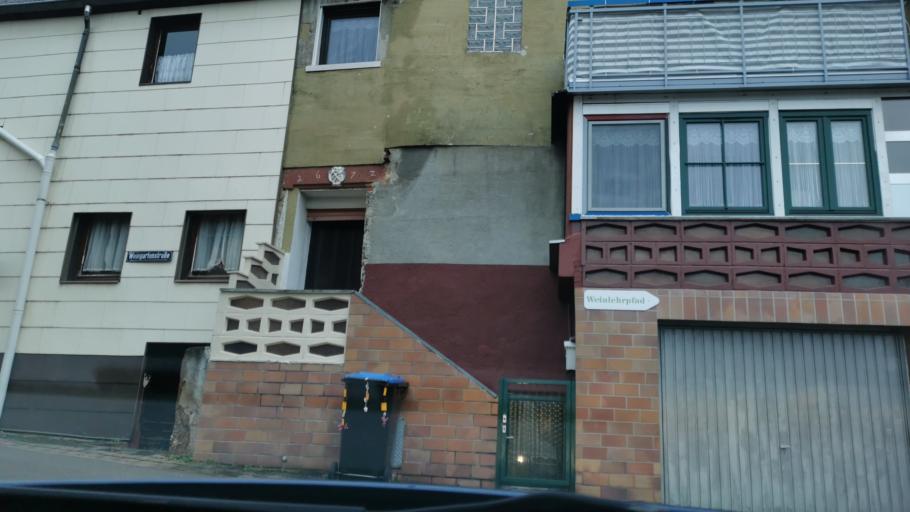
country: DE
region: Rheinland-Pfalz
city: Wintrich
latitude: 49.8808
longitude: 6.9530
